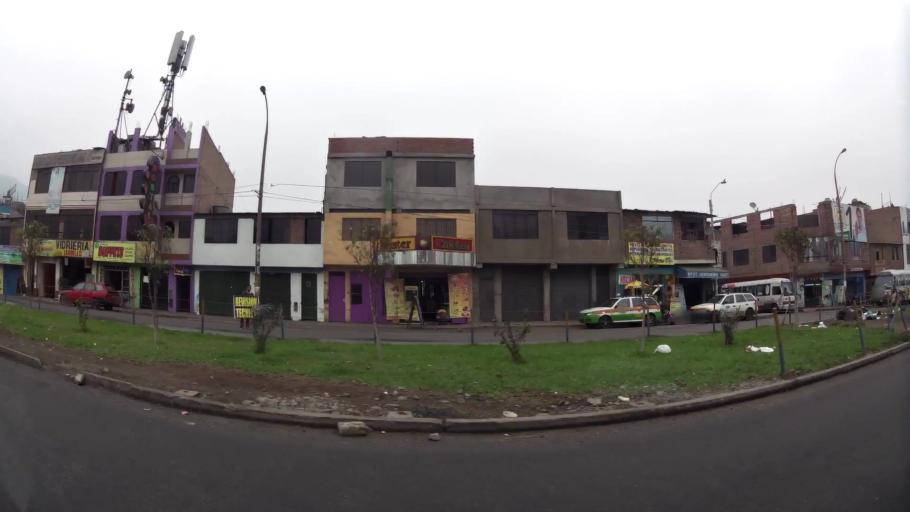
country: PE
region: Lima
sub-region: Lima
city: Urb. Santo Domingo
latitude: -11.9387
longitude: -76.9736
